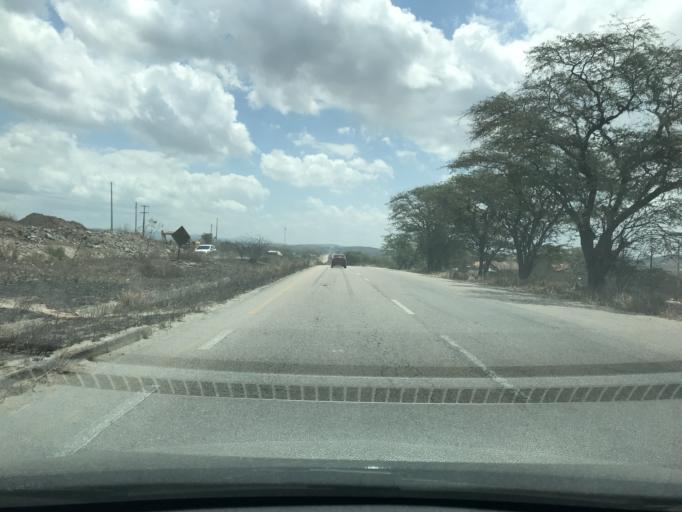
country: BR
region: Pernambuco
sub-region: Caruaru
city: Caruaru
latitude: -8.2960
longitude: -35.8919
